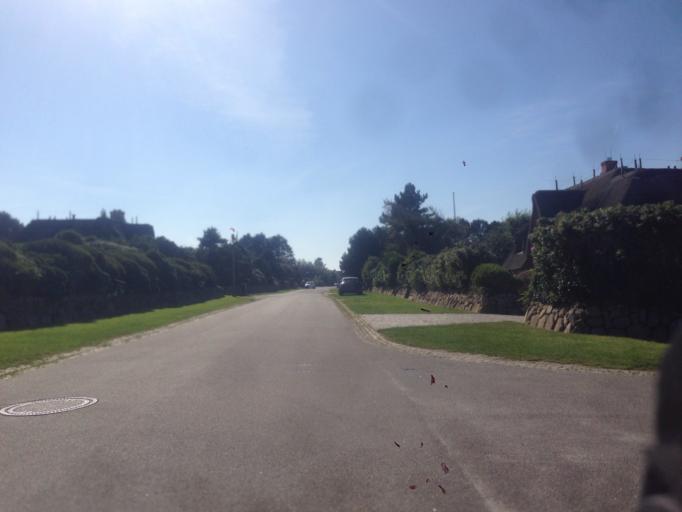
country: DE
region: Schleswig-Holstein
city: Tinnum
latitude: 54.9588
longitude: 8.3500
